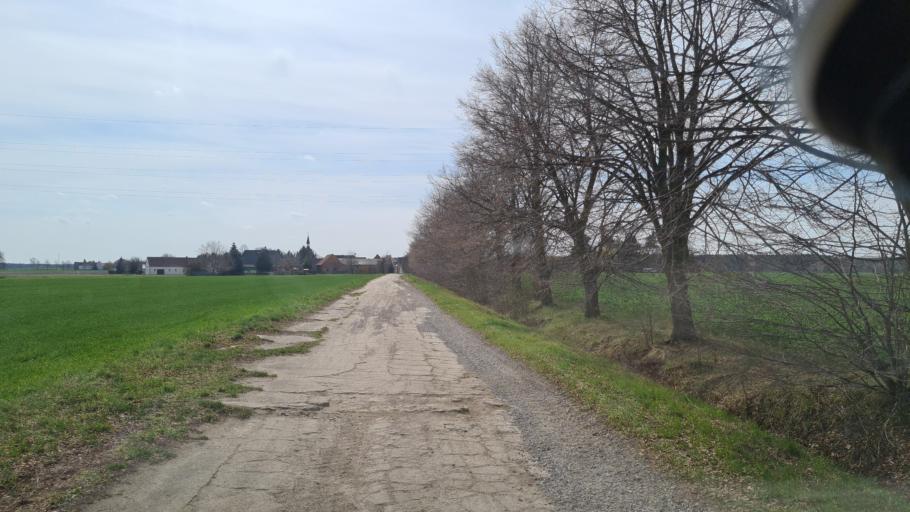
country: DE
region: Brandenburg
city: Bronkow
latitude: 51.5987
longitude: 13.9265
